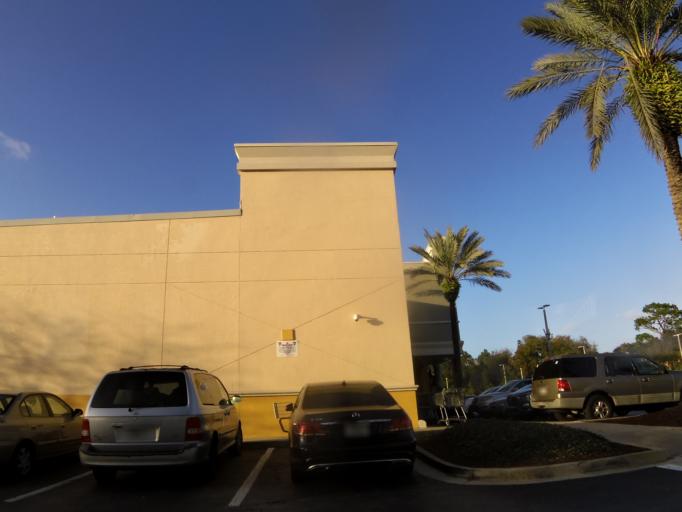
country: US
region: Florida
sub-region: Duval County
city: Jacksonville
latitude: 30.2677
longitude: -81.5607
